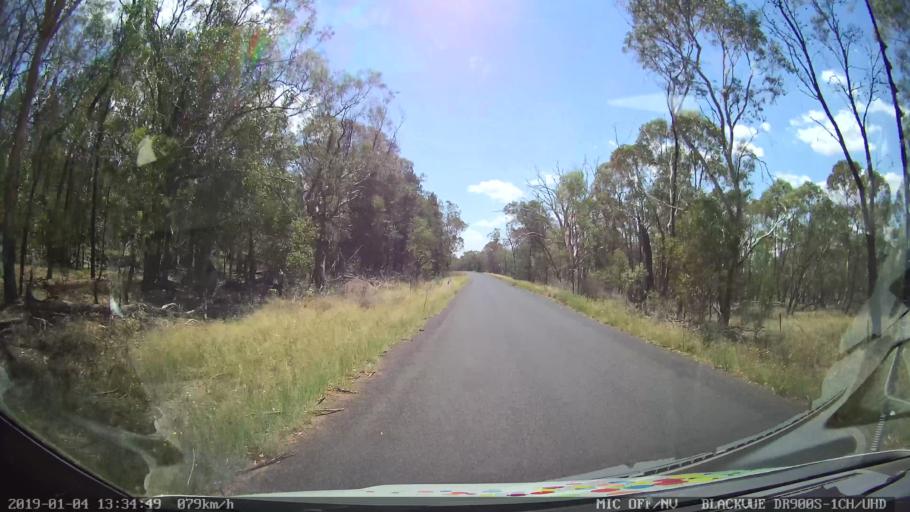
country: AU
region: New South Wales
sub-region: Dubbo Municipality
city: Dubbo
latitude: -32.5808
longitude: 148.5363
